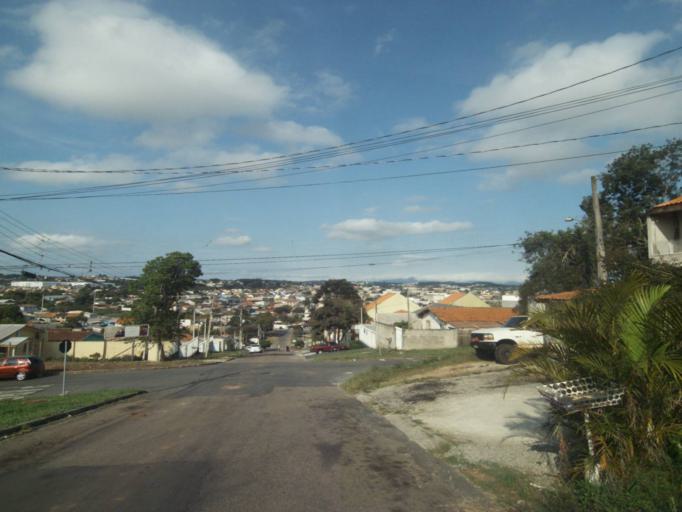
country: BR
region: Parana
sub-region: Pinhais
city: Pinhais
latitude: -25.4044
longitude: -49.1974
